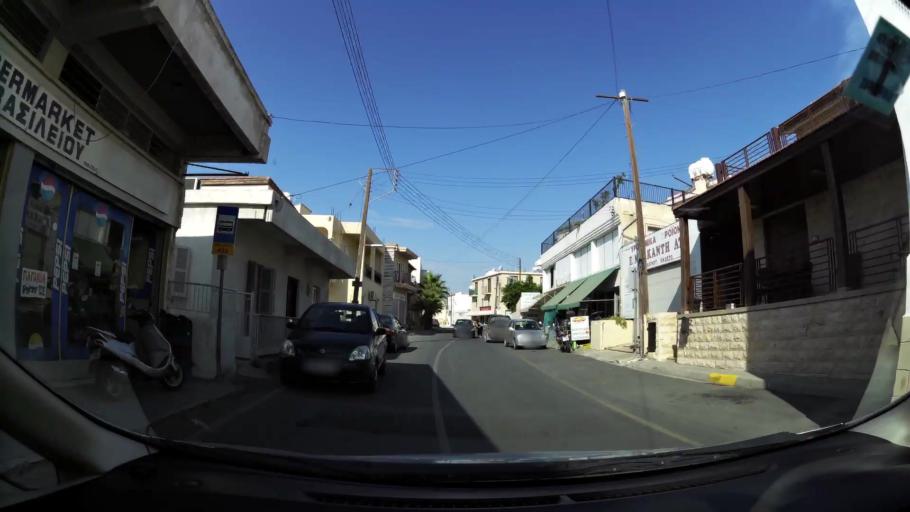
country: CY
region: Larnaka
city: Aradippou
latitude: 34.9525
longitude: 33.5900
